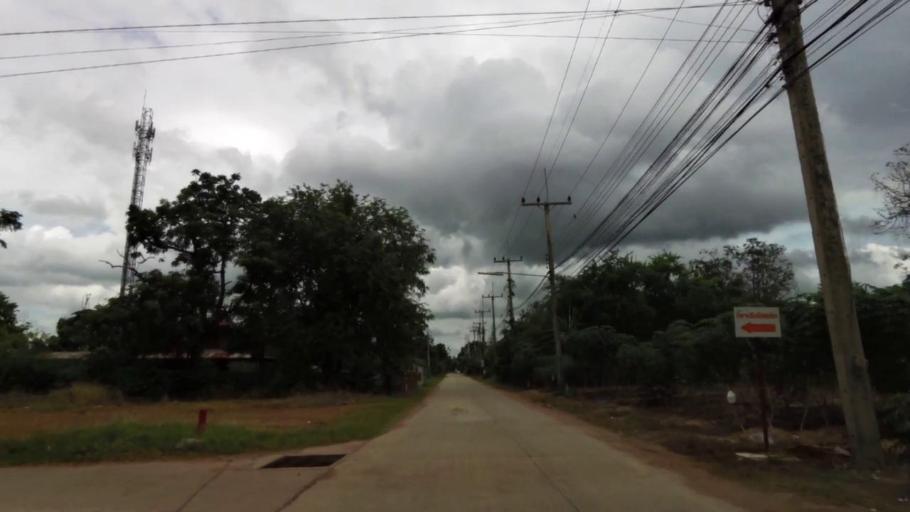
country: TH
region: Nakhon Sawan
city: Phai Sali
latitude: 15.6009
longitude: 100.6624
